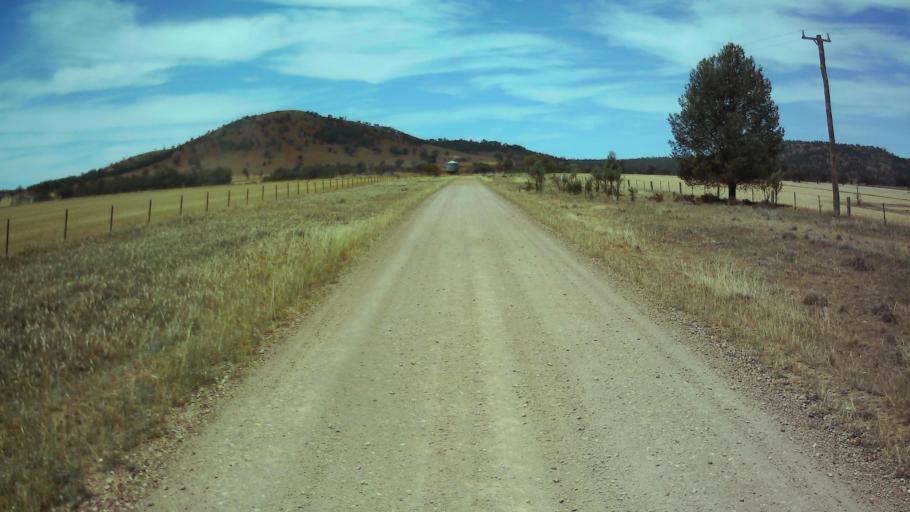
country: AU
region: New South Wales
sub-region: Weddin
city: Grenfell
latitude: -33.7625
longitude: 148.1359
